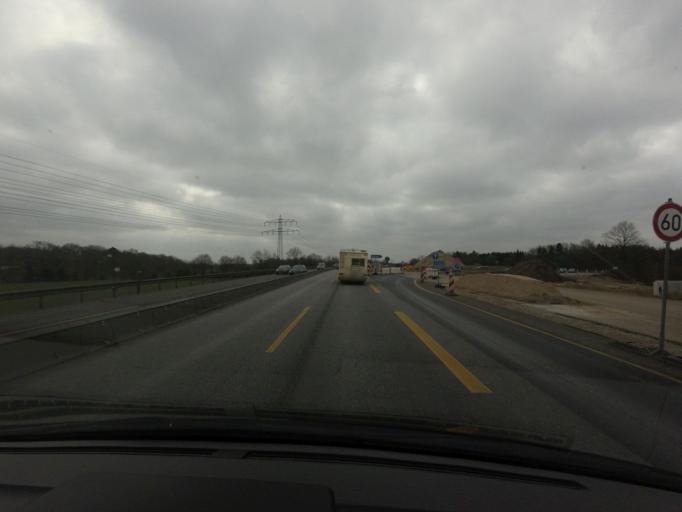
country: DE
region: Schleswig-Holstein
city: Bonningstedt
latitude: 53.6477
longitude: 9.9306
